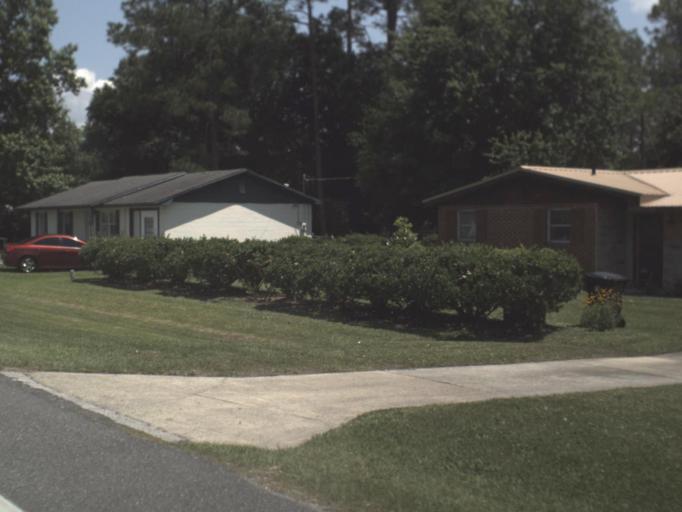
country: US
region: Florida
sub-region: Bradford County
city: Starke
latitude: 29.9338
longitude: -82.1043
